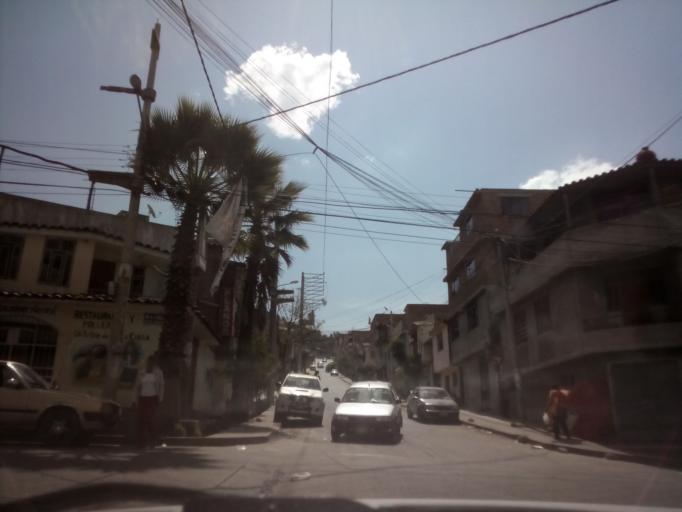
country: PE
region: Ayacucho
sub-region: Provincia de Huamanga
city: Ayacucho
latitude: -13.1487
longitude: -74.2303
